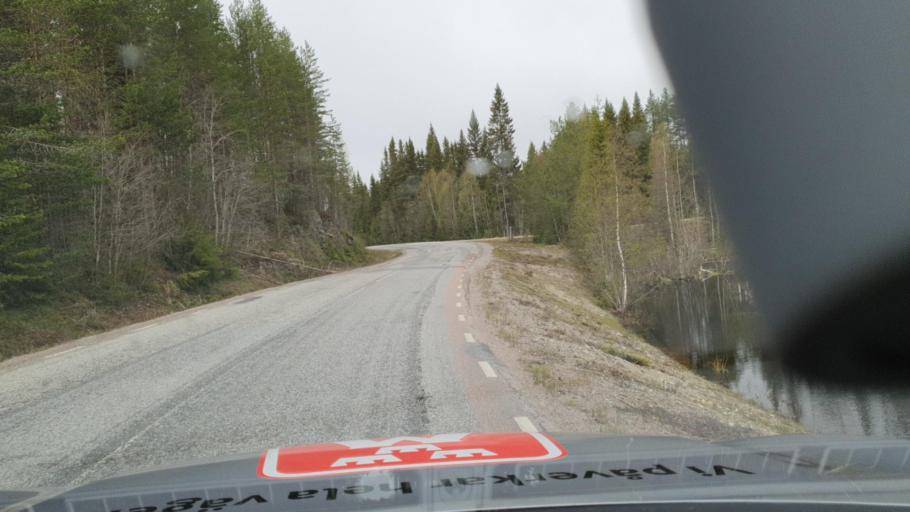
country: SE
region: Vaesterbotten
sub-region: Asele Kommun
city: Asele
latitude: 63.7031
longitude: 17.2036
